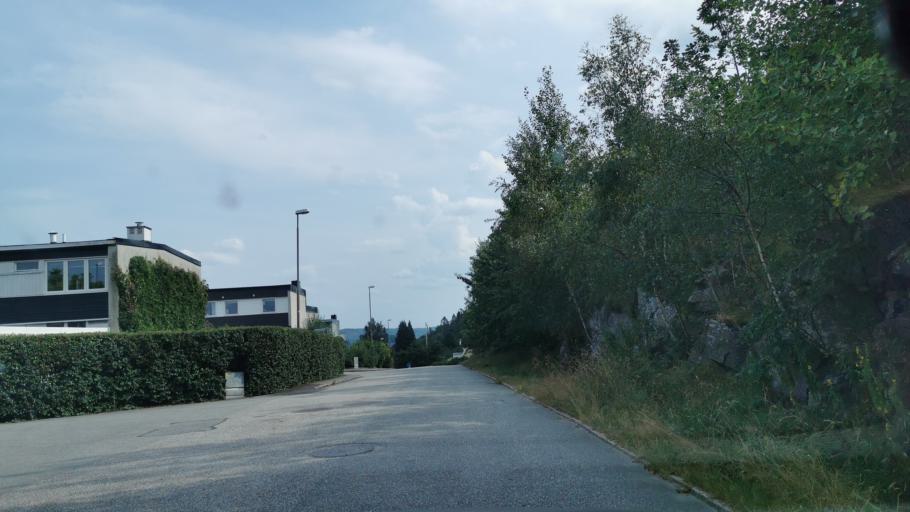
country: SE
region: Vaestra Goetaland
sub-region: Molndal
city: Moelndal
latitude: 57.6683
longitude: 11.9811
